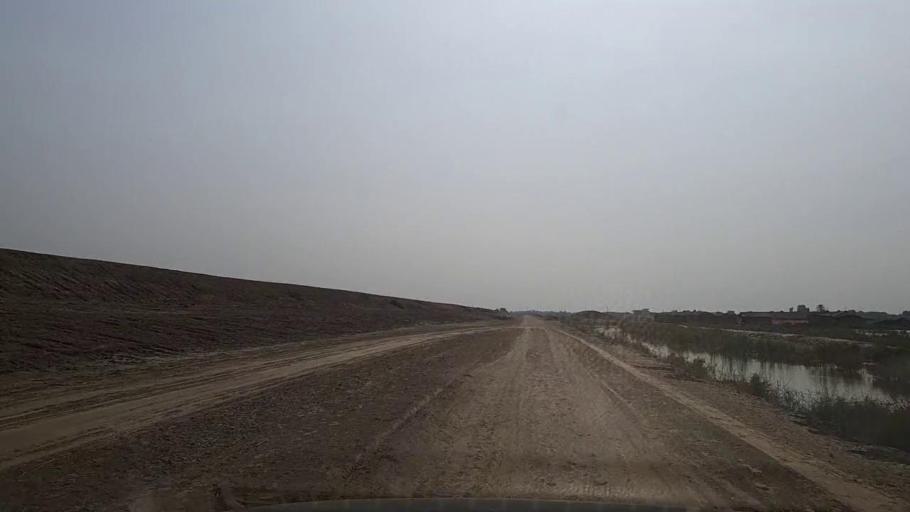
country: PK
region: Sindh
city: Thatta
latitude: 24.5691
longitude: 67.9133
